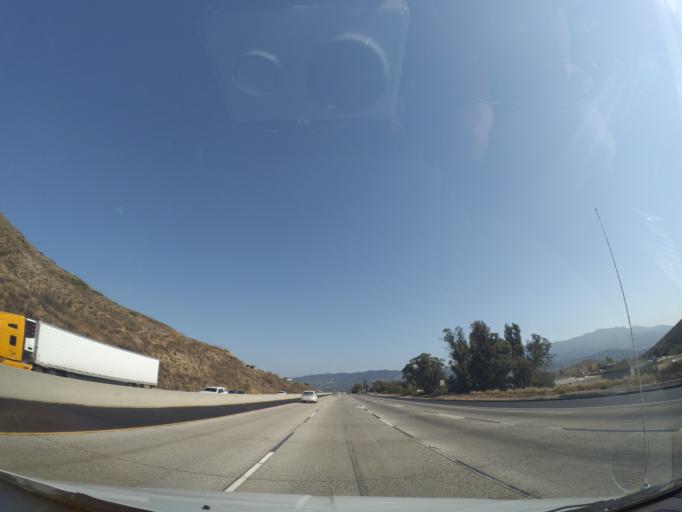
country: US
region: California
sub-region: Ventura County
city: Casa Conejo
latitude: 34.1972
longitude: -118.9527
